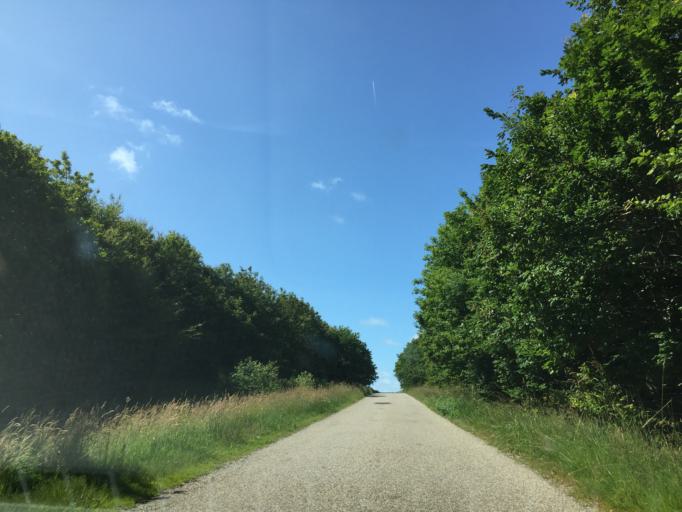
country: DK
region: North Denmark
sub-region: Thisted Kommune
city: Hurup
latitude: 56.7013
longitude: 8.4380
